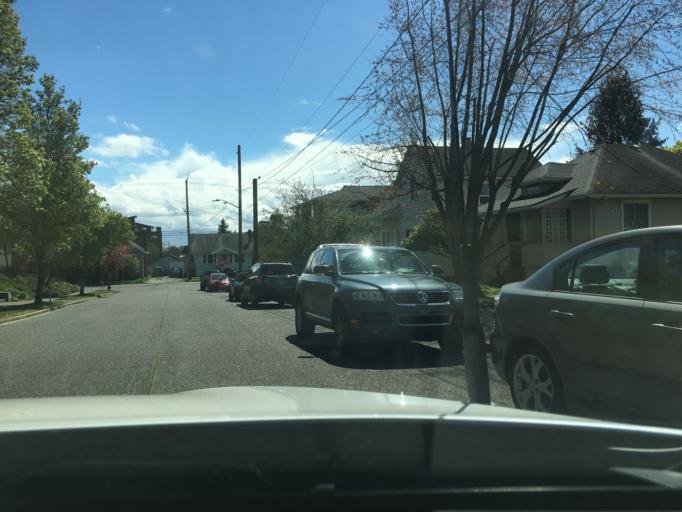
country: US
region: Washington
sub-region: King County
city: Seattle
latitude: 47.6766
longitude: -122.3811
